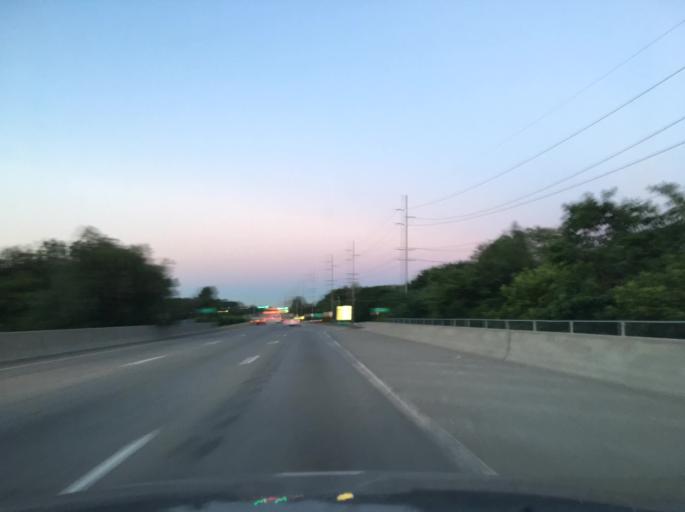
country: US
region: Michigan
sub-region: Macomb County
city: Mount Clemens
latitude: 42.6284
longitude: -82.8896
